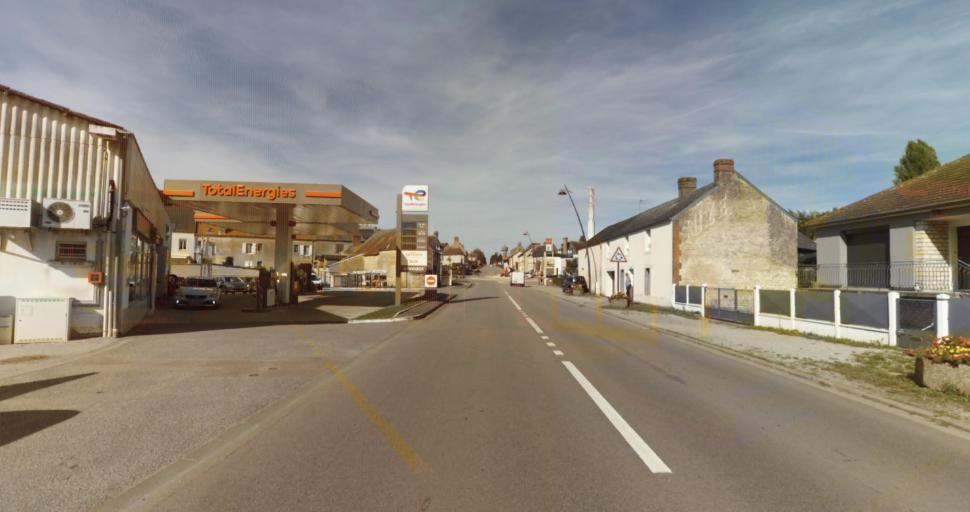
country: FR
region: Lower Normandy
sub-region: Departement de l'Orne
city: Sees
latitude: 48.7061
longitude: 0.2227
